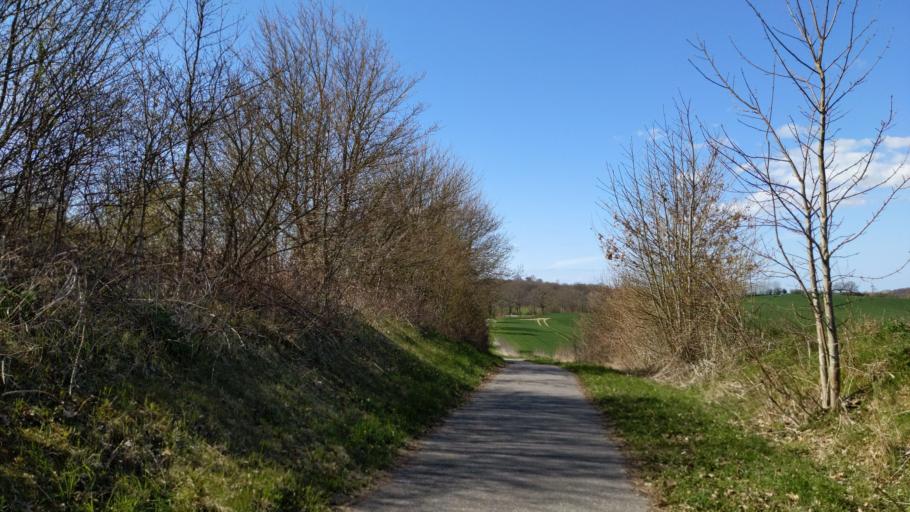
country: DE
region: Schleswig-Holstein
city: Susel
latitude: 54.1077
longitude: 10.7024
